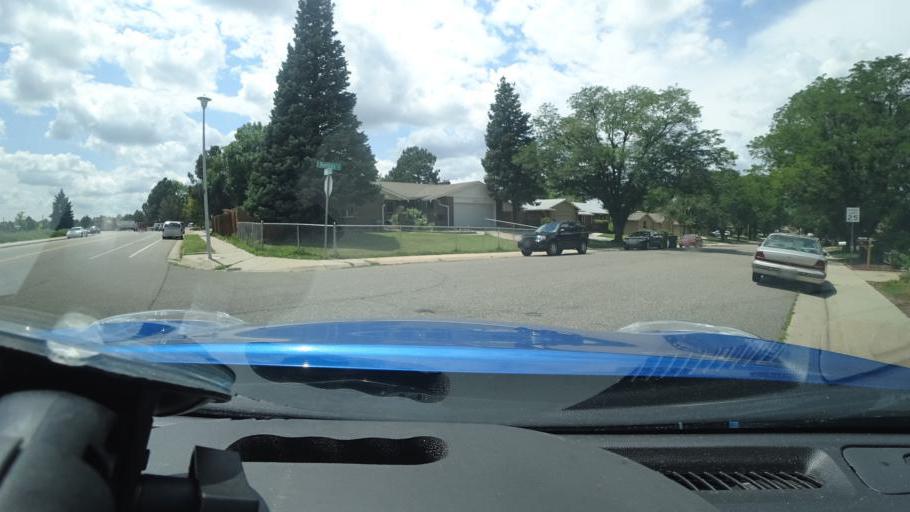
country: US
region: Colorado
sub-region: Adams County
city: Aurora
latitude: 39.7000
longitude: -104.8404
